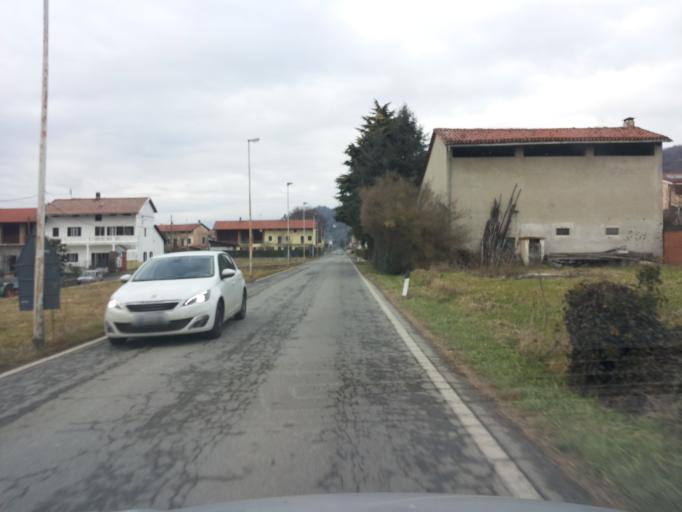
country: IT
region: Piedmont
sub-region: Provincia di Torino
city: Borgomasino
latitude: 45.3664
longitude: 7.9843
